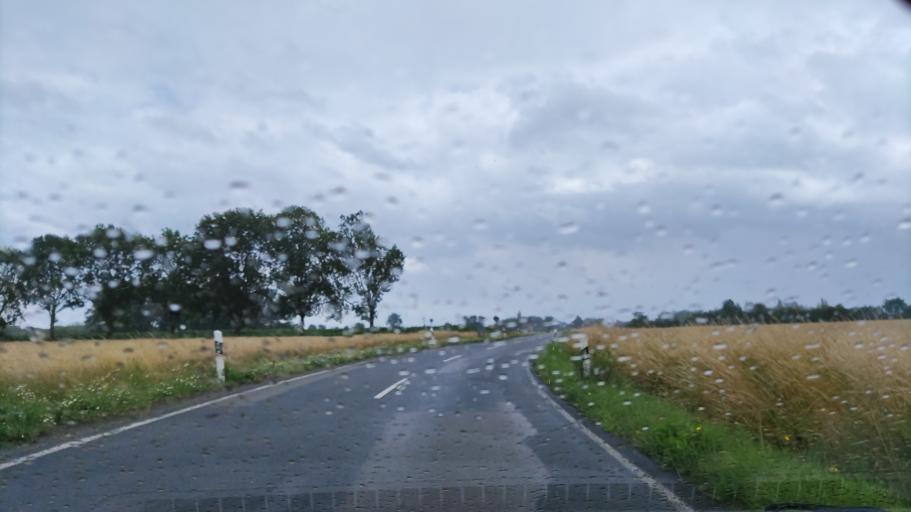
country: DE
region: North Rhine-Westphalia
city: Sendenhorst
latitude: 51.8044
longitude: 7.8295
